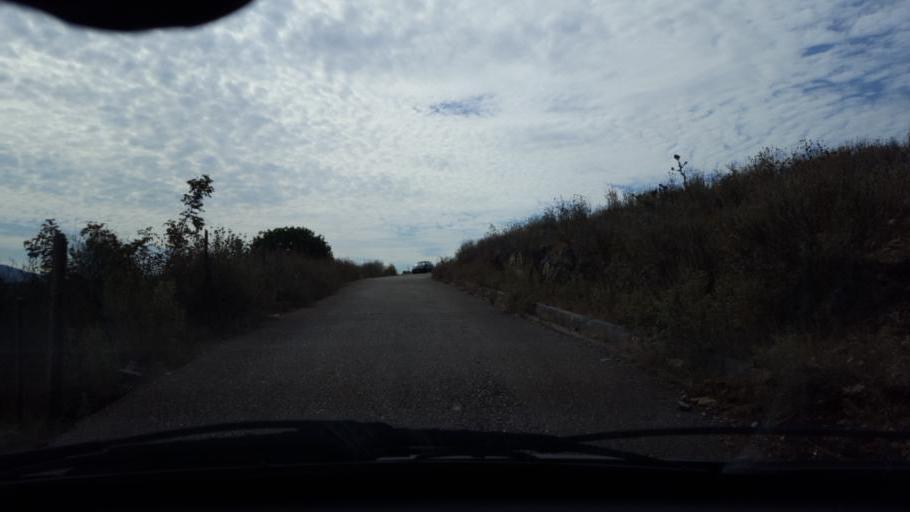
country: AL
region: Vlore
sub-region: Rrethi i Sarandes
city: Xarre
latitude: 39.7601
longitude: 19.9889
